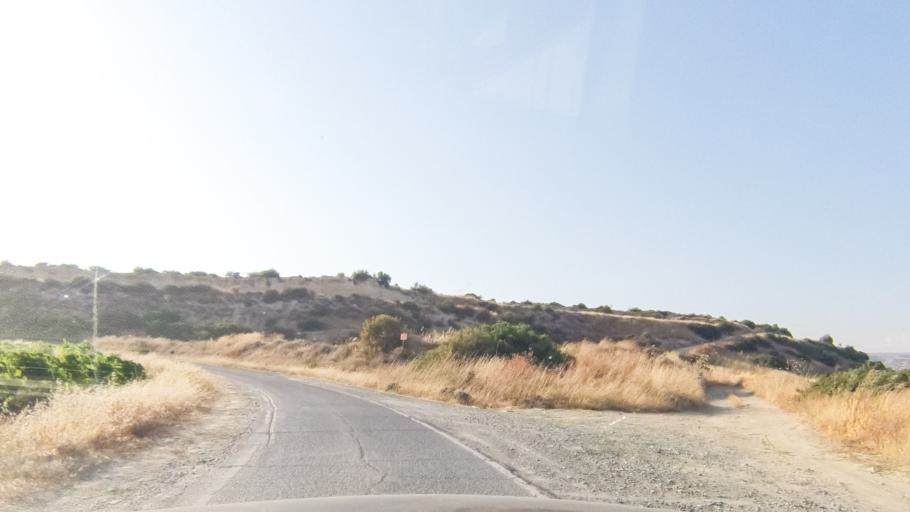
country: CY
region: Limassol
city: Pissouri
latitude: 34.6736
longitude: 32.7668
